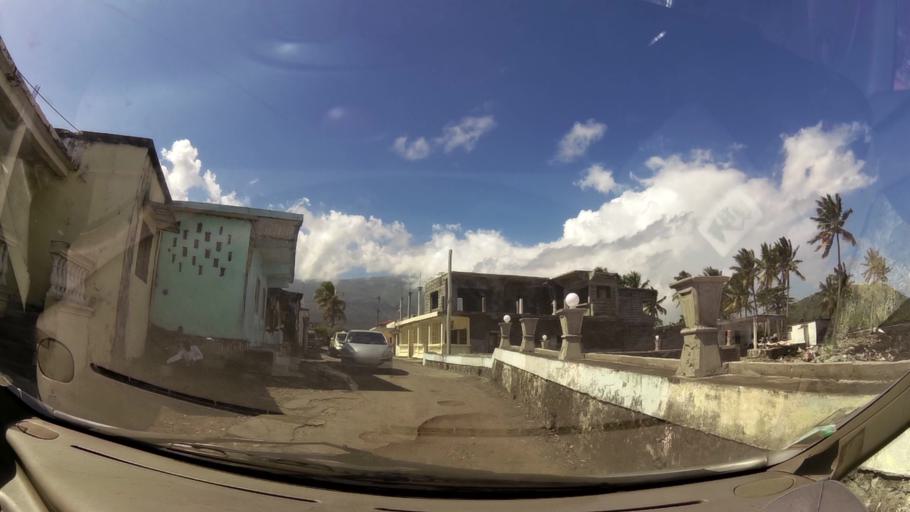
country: KM
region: Grande Comore
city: Mavingouni
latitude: -11.7464
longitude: 43.2318
